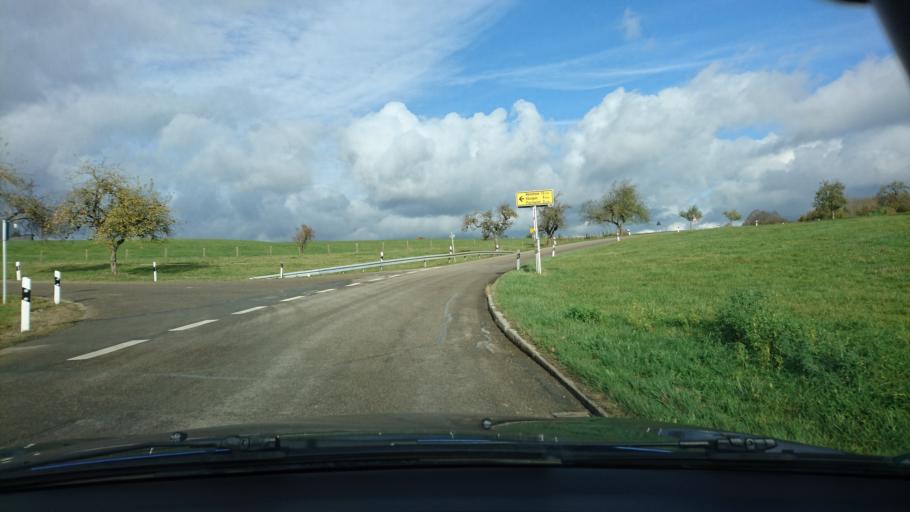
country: DE
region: Bavaria
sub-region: Swabia
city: Forheim
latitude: 48.7517
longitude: 10.4676
